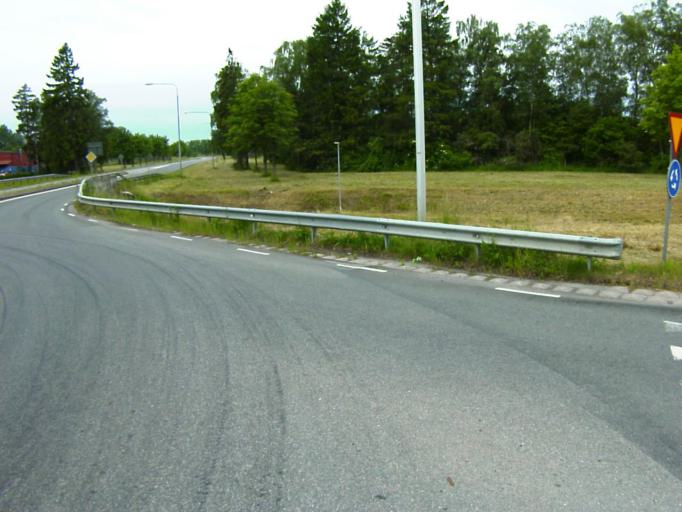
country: SE
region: Skane
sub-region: Kristianstads Kommun
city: Kristianstad
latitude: 56.0430
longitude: 14.1514
